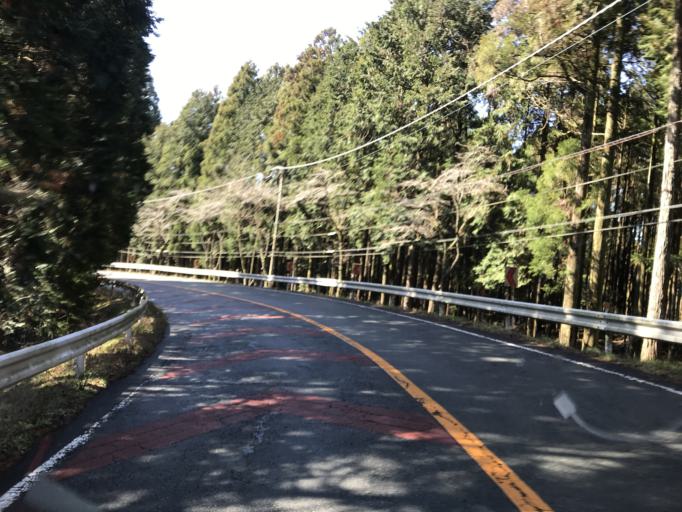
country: JP
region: Shizuoka
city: Fujinomiya
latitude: 35.2907
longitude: 138.6617
